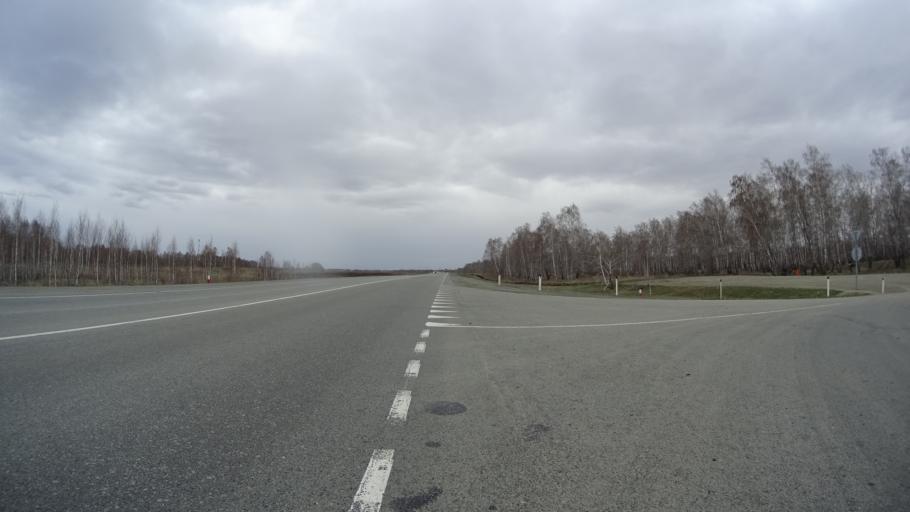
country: RU
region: Chelyabinsk
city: Krasnogorskiy
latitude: 54.6927
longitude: 61.2492
